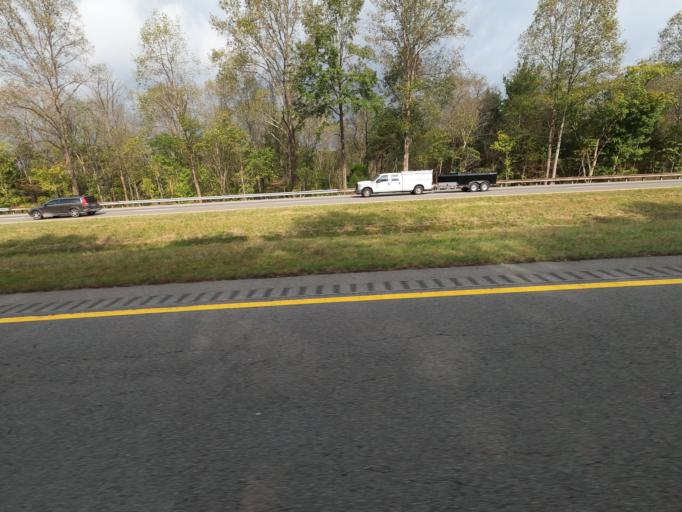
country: US
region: Tennessee
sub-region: Dickson County
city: Burns
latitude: 36.0193
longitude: -87.2354
